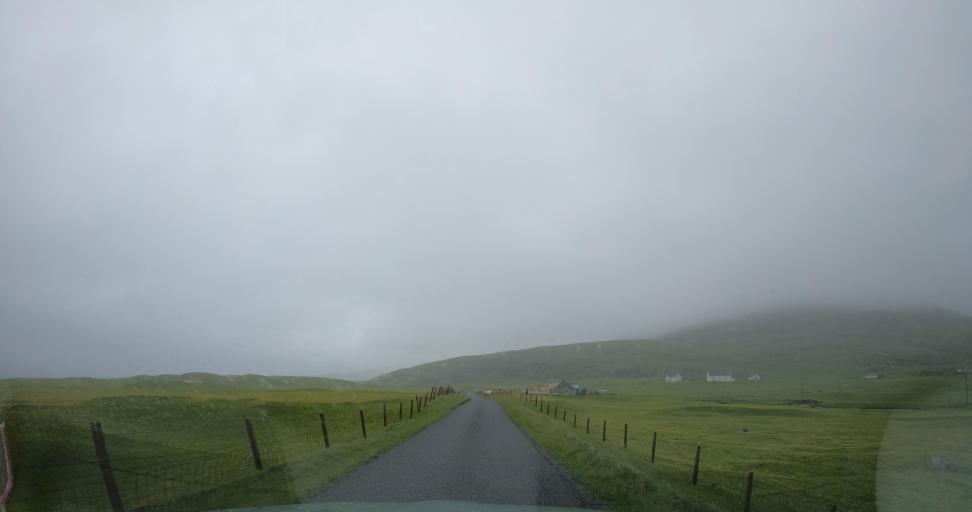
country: GB
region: Scotland
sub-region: Eilean Siar
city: Barra
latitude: 56.9838
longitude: -7.5099
